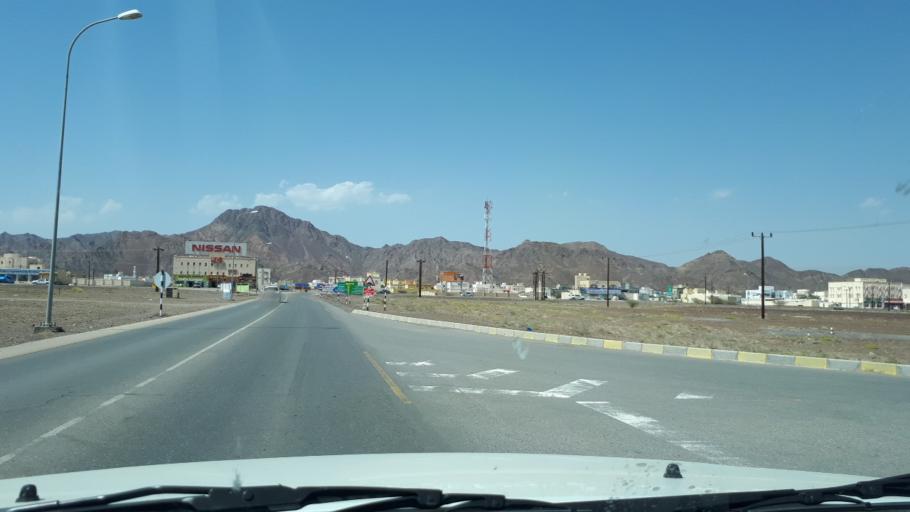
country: OM
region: Muhafazat ad Dakhiliyah
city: Bahla'
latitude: 22.9456
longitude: 57.2597
